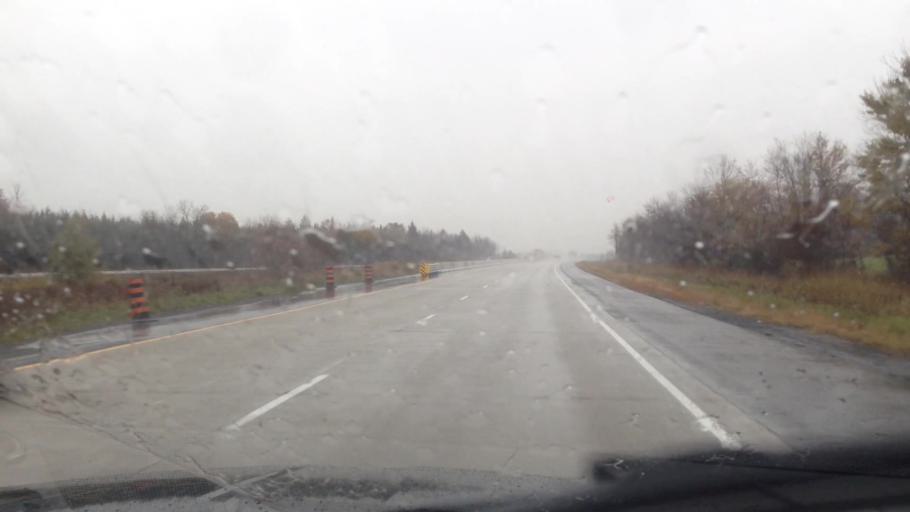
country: CA
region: Ontario
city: Hawkesbury
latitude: 45.5048
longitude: -74.5874
